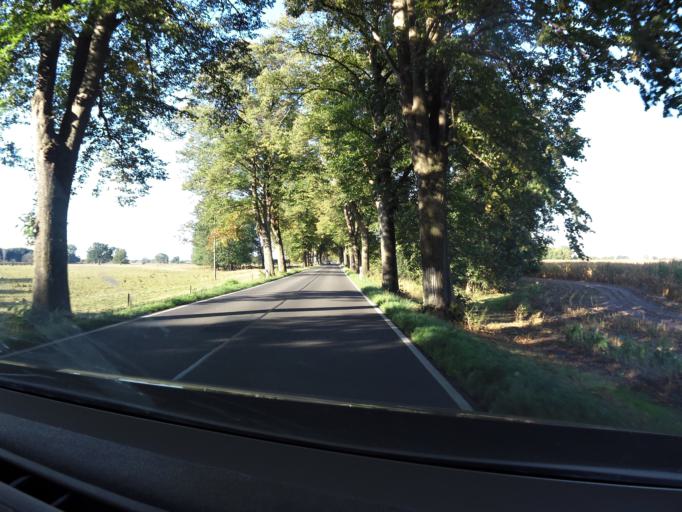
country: DE
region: Mecklenburg-Vorpommern
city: Alt-Sanitz
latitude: 53.8427
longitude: 13.5947
